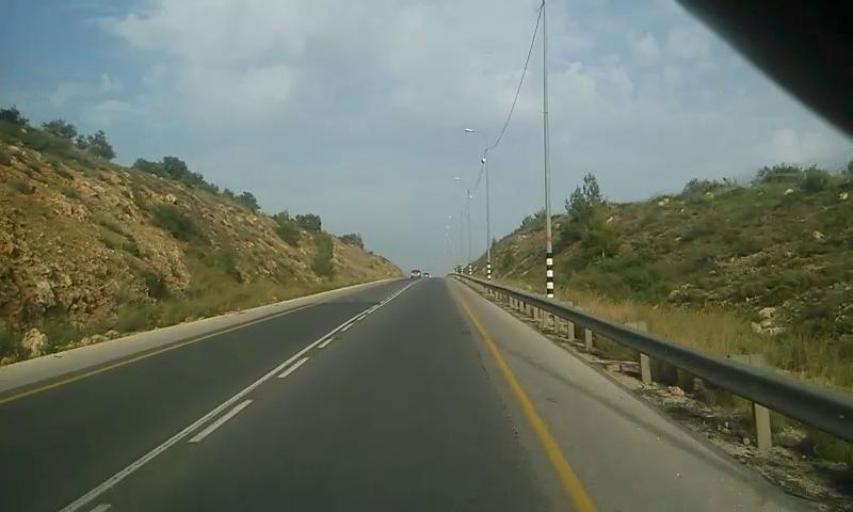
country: PS
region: West Bank
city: `Azzun
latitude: 32.1818
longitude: 35.0460
